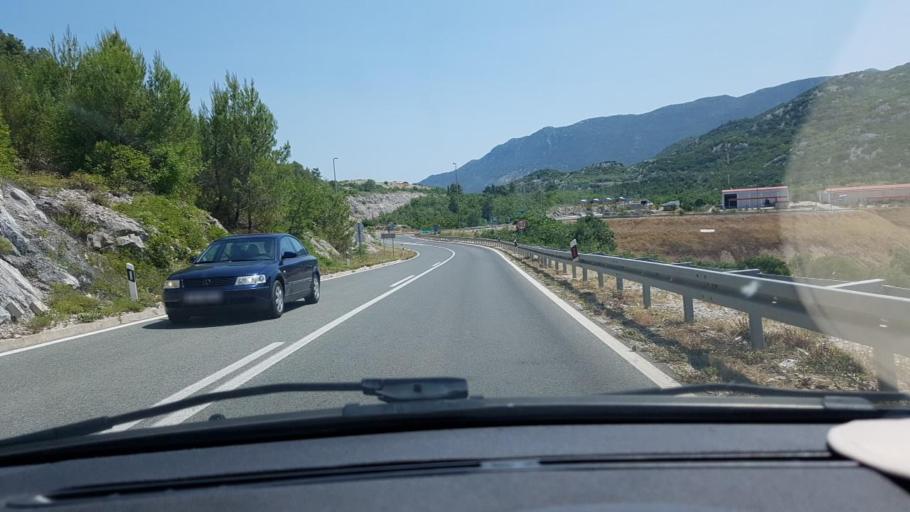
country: HR
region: Splitsko-Dalmatinska
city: Vrgorac
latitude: 43.1949
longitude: 17.3788
